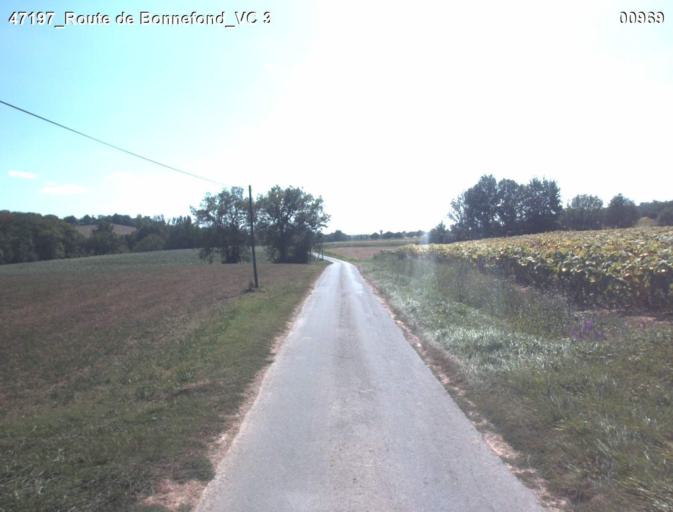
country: FR
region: Aquitaine
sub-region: Departement du Lot-et-Garonne
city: Laplume
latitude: 44.1039
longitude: 0.4754
